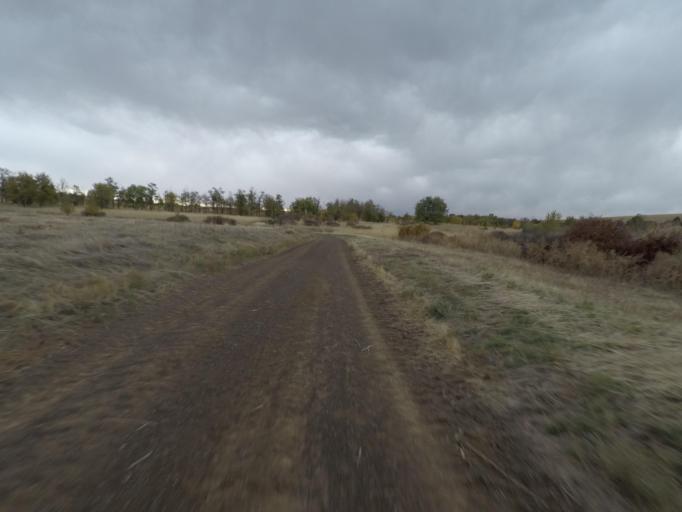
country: US
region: Washington
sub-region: Walla Walla County
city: Walla Walla East
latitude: 46.0745
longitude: -118.2570
